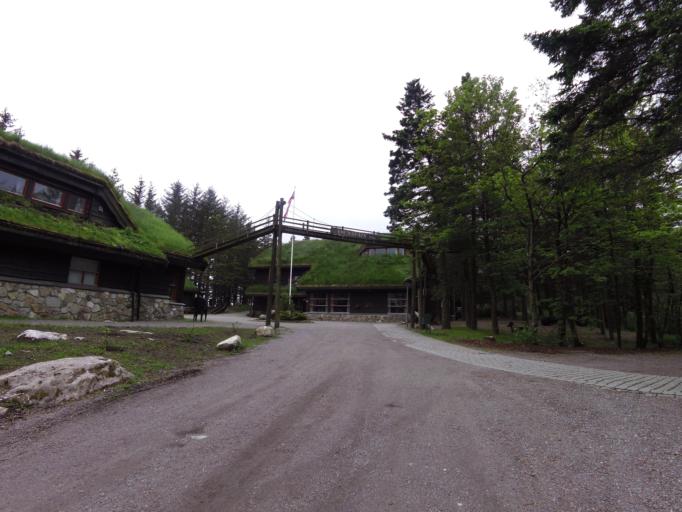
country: NO
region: Rogaland
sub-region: Ha
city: Vigrestad
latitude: 58.6256
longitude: 5.7753
